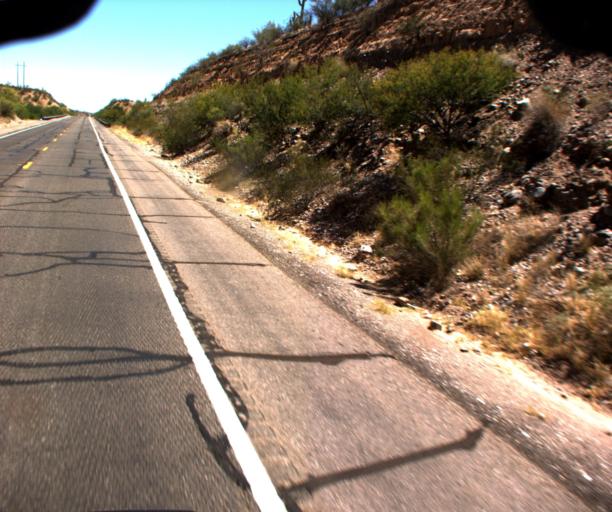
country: US
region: Arizona
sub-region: Pinal County
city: Mammoth
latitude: 32.7636
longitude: -110.6542
